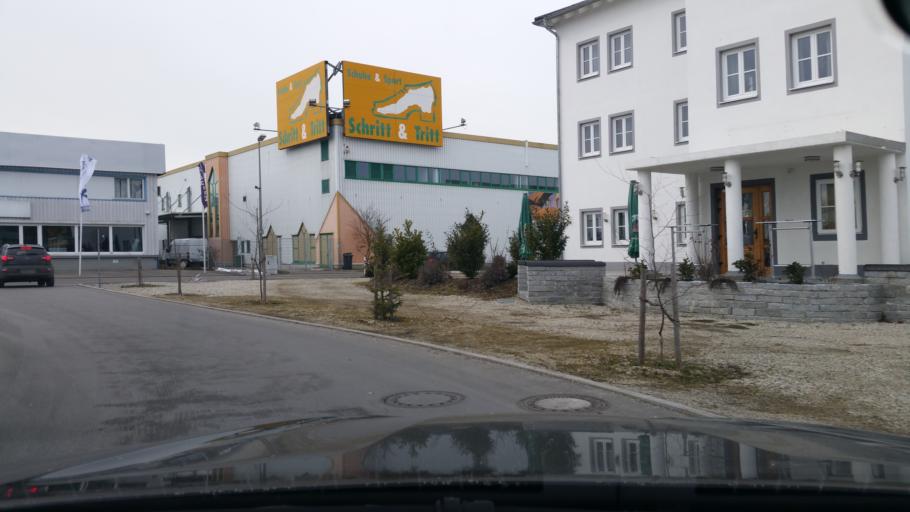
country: DE
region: Bavaria
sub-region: Lower Bavaria
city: Bruckberg
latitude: 48.4861
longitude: 12.0145
